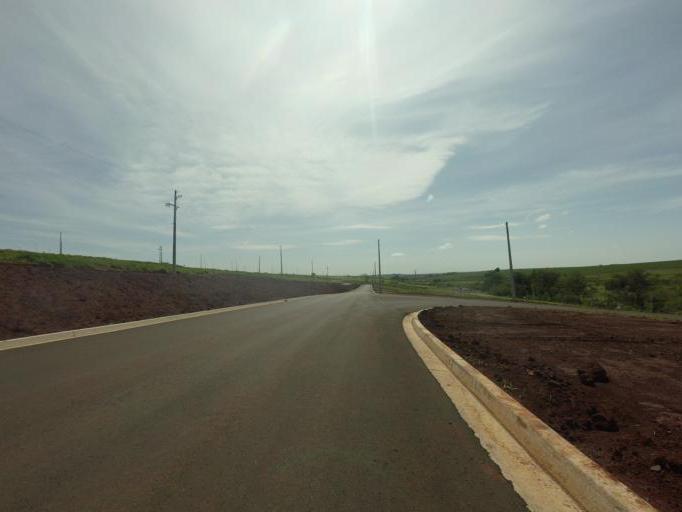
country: BR
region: Sao Paulo
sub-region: Piracicaba
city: Piracicaba
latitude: -22.7639
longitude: -47.5825
